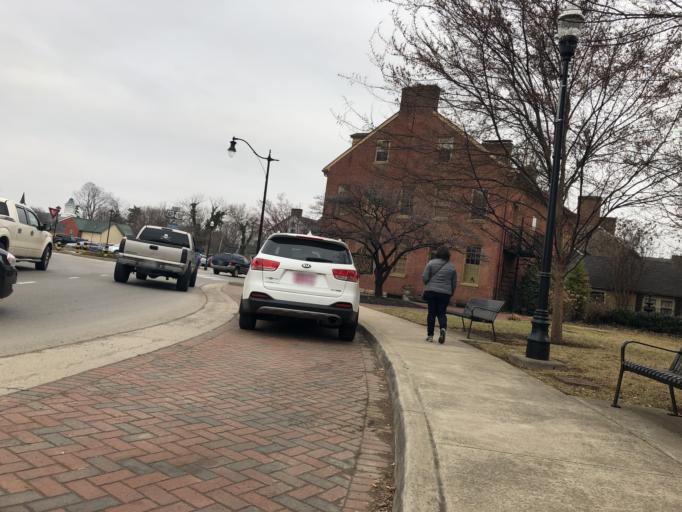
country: US
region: Kentucky
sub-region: Nelson County
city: Bardstown
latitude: 37.8088
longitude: -85.4668
